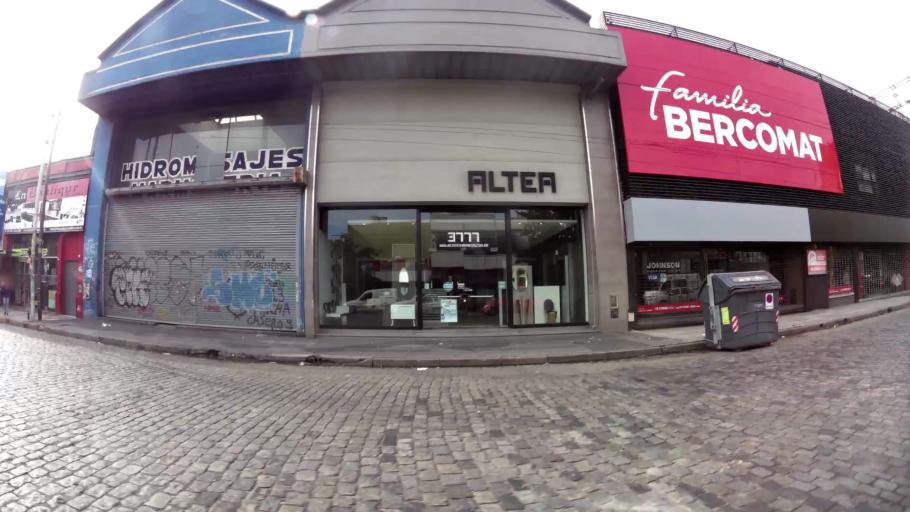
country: AR
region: Buenos Aires F.D.
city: Villa Santa Rita
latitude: -34.6368
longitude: -58.4782
